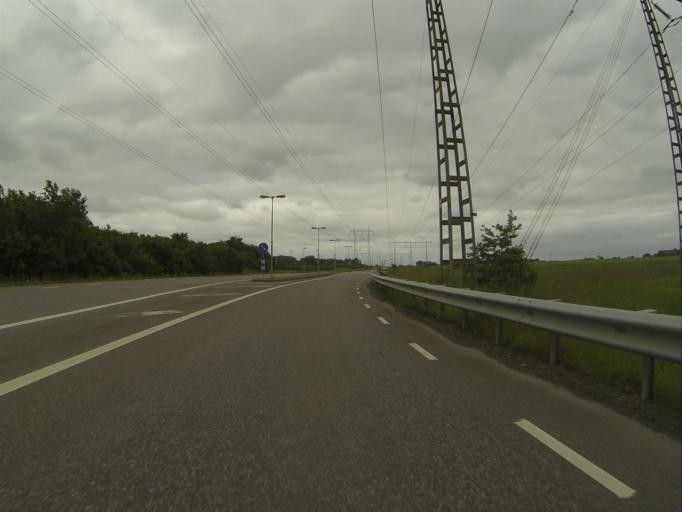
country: SE
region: Skane
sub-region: Staffanstorps Kommun
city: Staffanstorp
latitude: 55.6496
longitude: 13.1980
